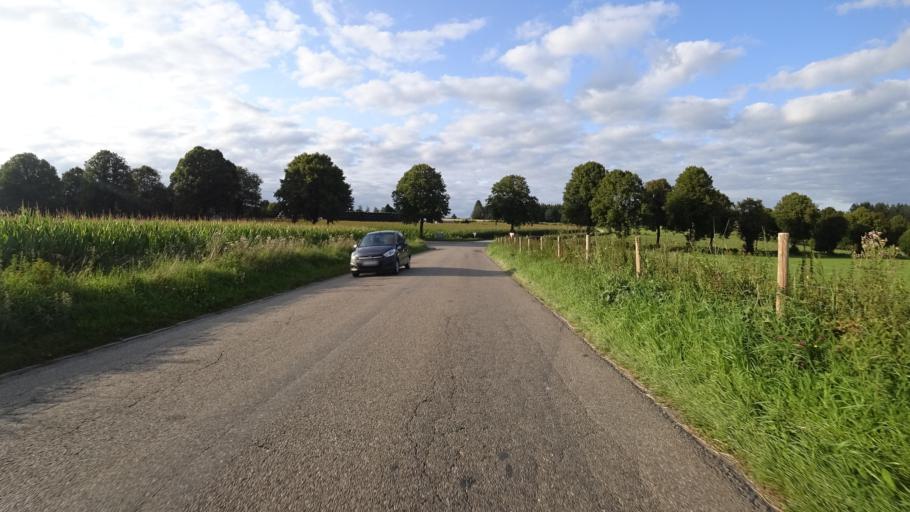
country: BE
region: Wallonia
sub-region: Province du Luxembourg
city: Bertrix
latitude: 49.8418
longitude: 5.3445
